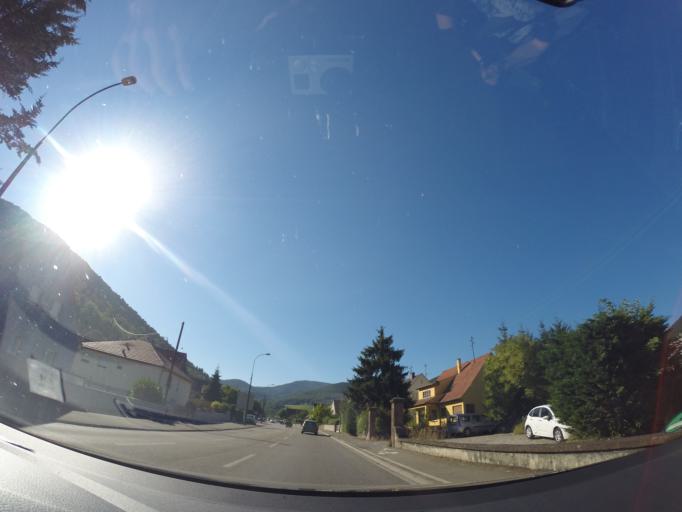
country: FR
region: Alsace
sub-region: Departement du Haut-Rhin
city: Kaysersberg
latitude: 48.1464
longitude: 7.2533
